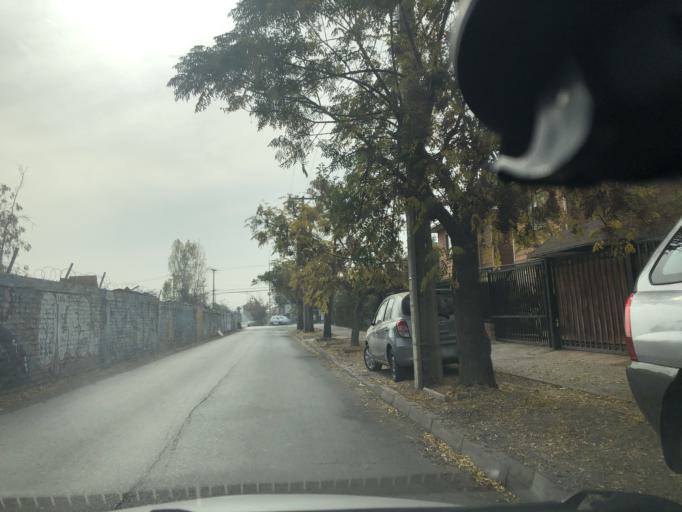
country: CL
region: Santiago Metropolitan
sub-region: Provincia de Cordillera
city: Puente Alto
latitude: -33.5775
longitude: -70.5764
